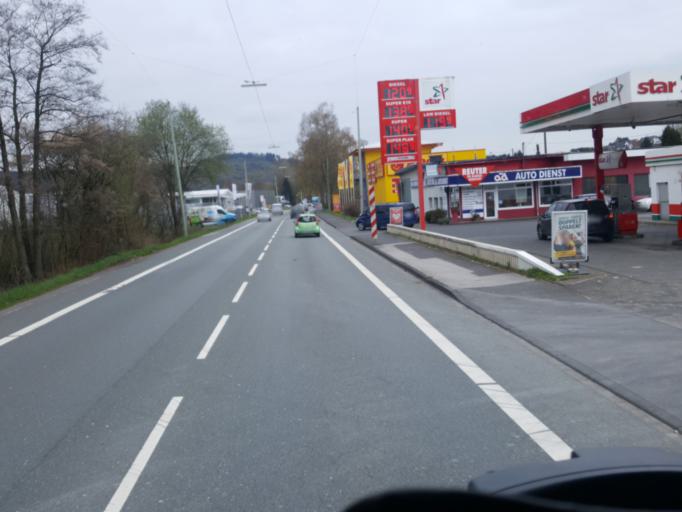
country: DE
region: North Rhine-Westphalia
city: Kreuztal
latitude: 50.9678
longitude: 8.0422
